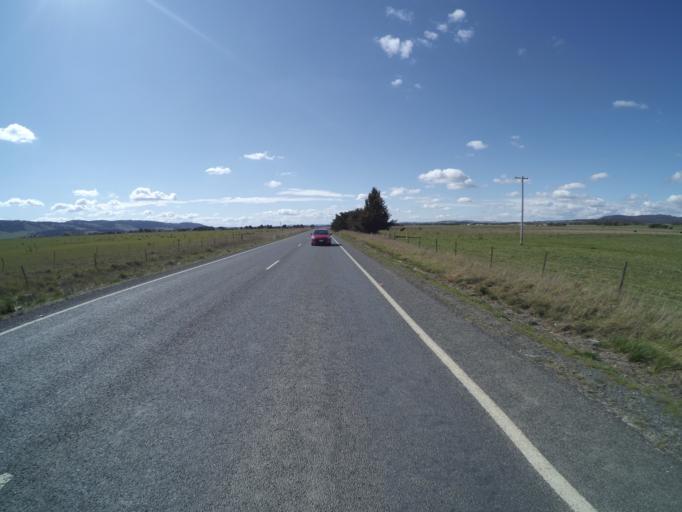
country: AU
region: New South Wales
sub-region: Palerang
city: Bungendore
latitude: -35.2822
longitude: 149.4221
